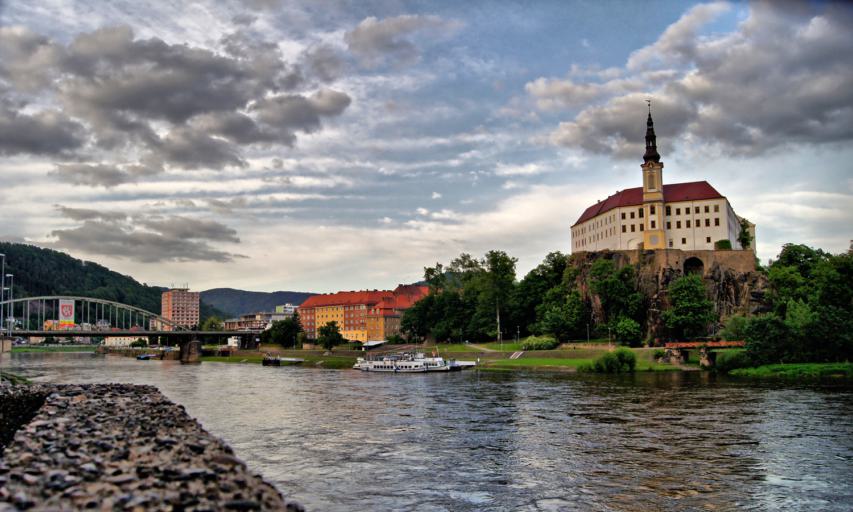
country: CZ
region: Ustecky
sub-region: Okres Decin
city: Decin
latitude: 50.7789
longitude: 14.2049
